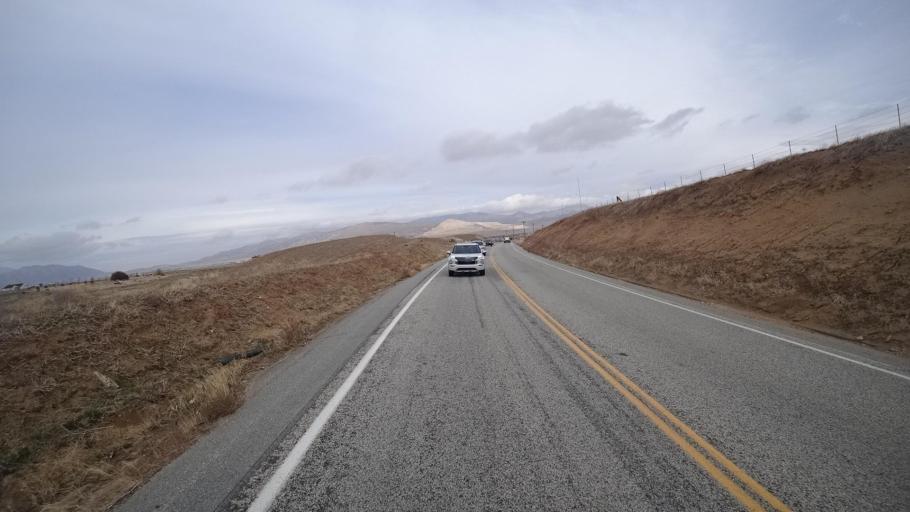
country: US
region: California
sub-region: Kern County
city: Tehachapi
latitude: 35.0909
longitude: -118.3969
